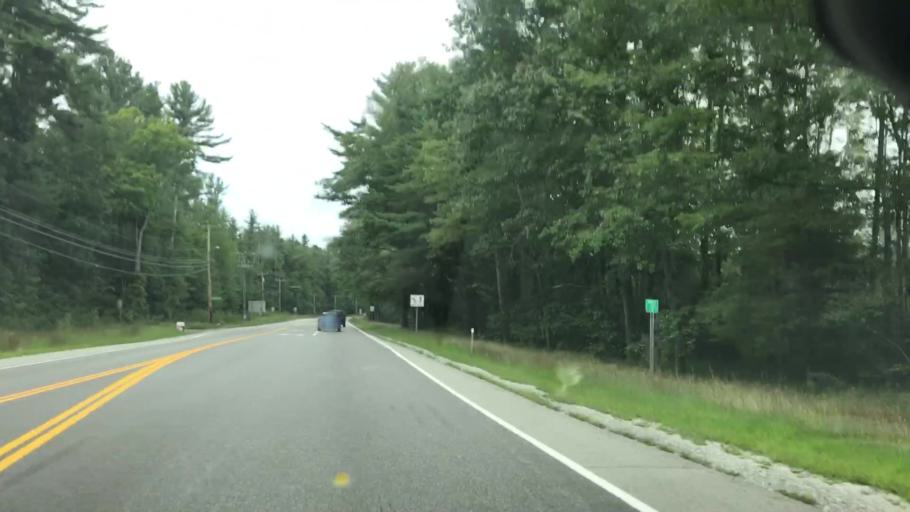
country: US
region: New Hampshire
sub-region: Hillsborough County
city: Milford
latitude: 42.8751
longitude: -71.6123
